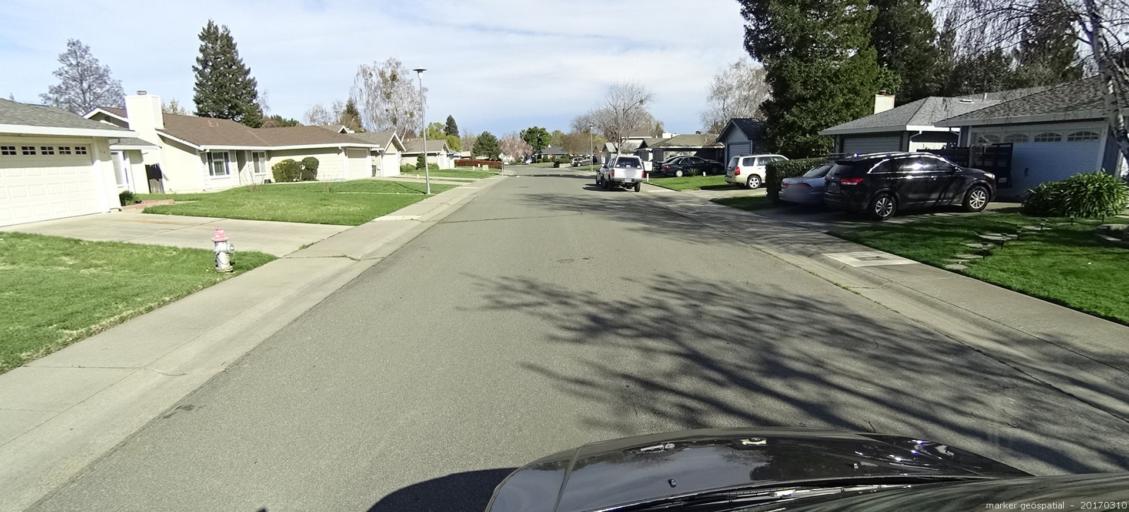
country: US
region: California
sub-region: Sacramento County
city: Parkway
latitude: 38.4890
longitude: -121.5406
